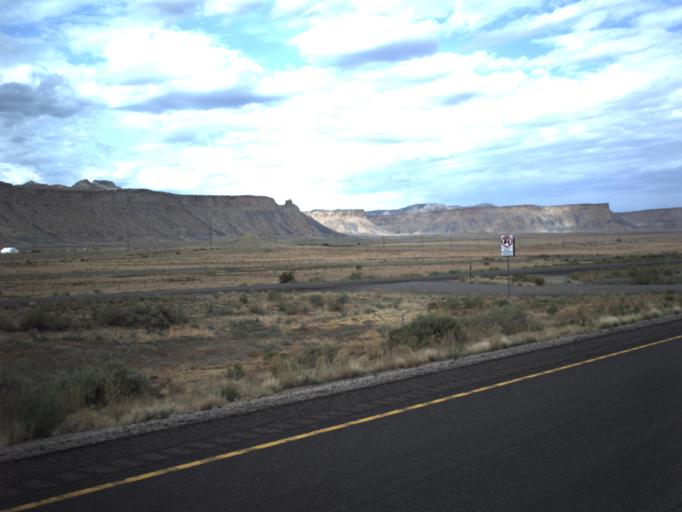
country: US
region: Utah
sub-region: Grand County
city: Moab
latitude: 38.9435
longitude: -109.8076
